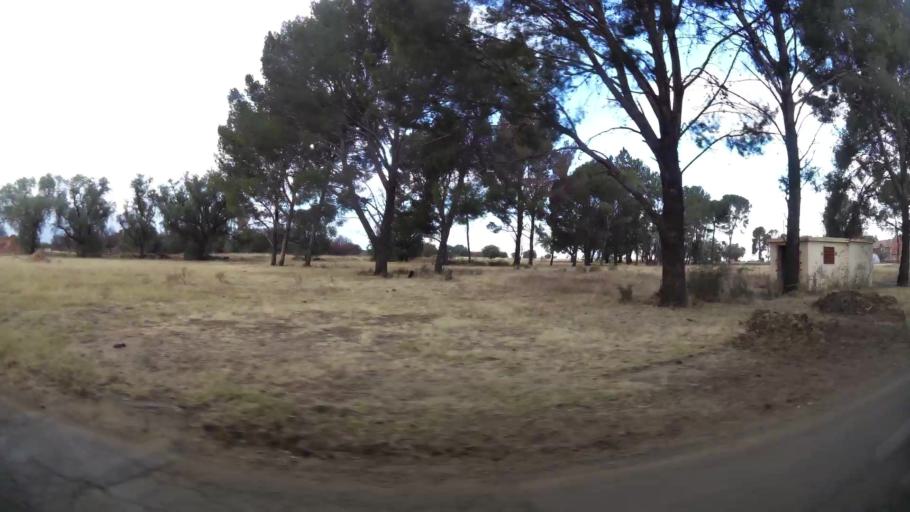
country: ZA
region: Orange Free State
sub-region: Lejweleputswa District Municipality
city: Welkom
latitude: -28.0133
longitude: 26.7155
